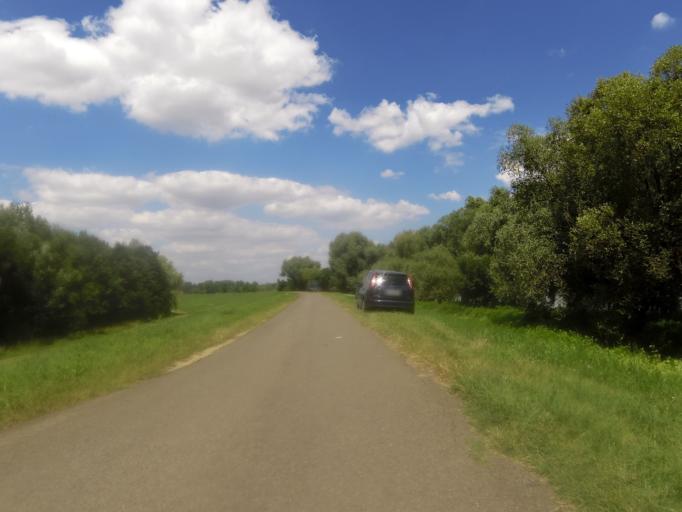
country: HU
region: Heves
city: Tiszanana
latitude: 47.5652
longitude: 20.6109
